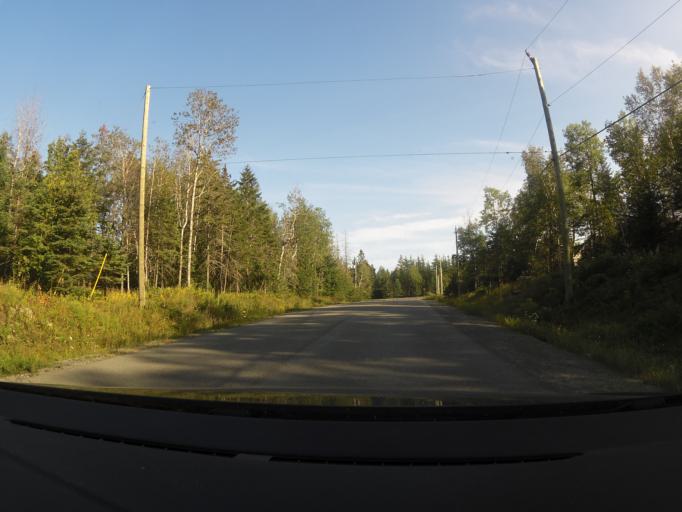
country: CA
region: Ontario
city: Carleton Place
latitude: 45.2933
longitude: -76.1069
